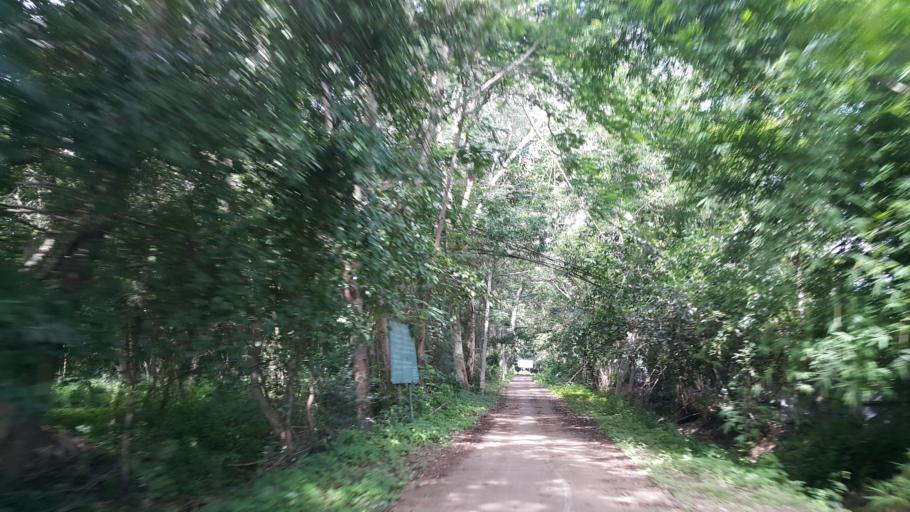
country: TH
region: Chiang Mai
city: Mae On
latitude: 18.7440
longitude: 99.1963
